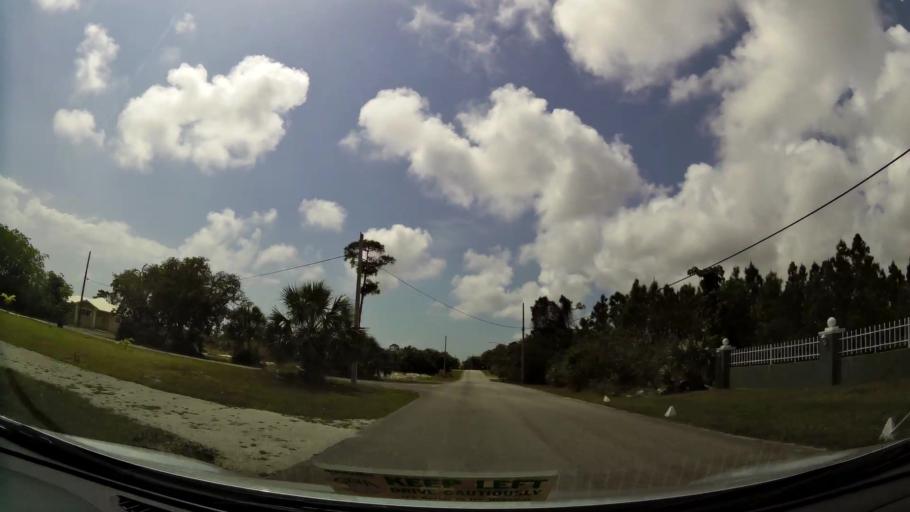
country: BS
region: Freeport
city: Freeport
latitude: 26.5154
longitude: -78.7110
